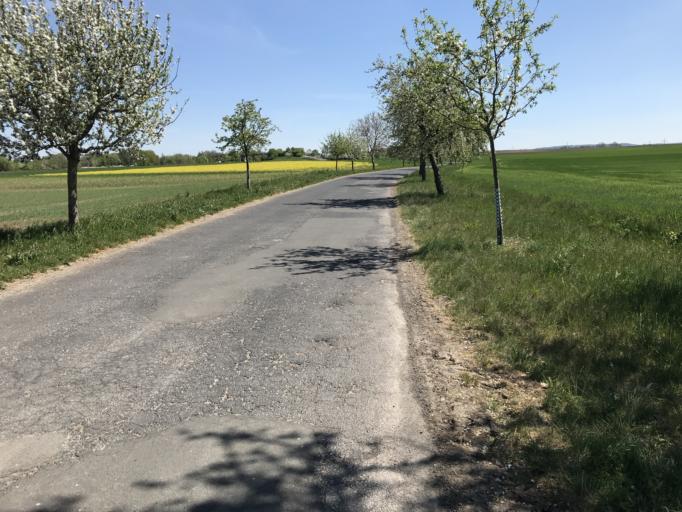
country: DE
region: Bavaria
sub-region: Regierungsbezirk Unterfranken
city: Markt Einersheim
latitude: 49.6876
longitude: 10.2728
